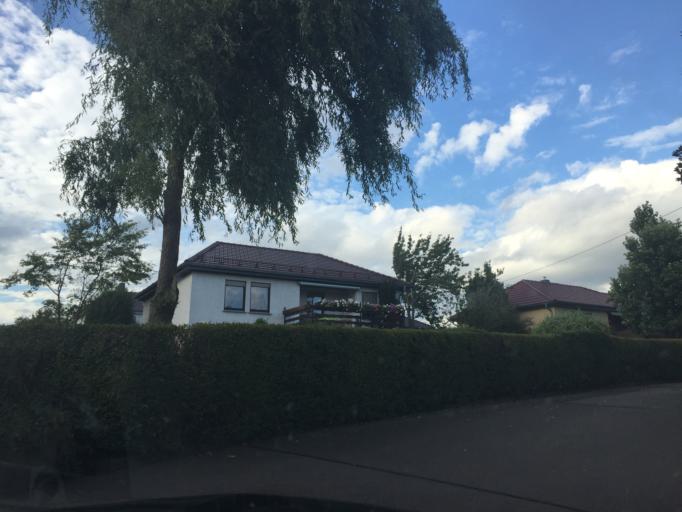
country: DE
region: Thuringia
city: Schmolln
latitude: 50.9145
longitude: 12.3528
